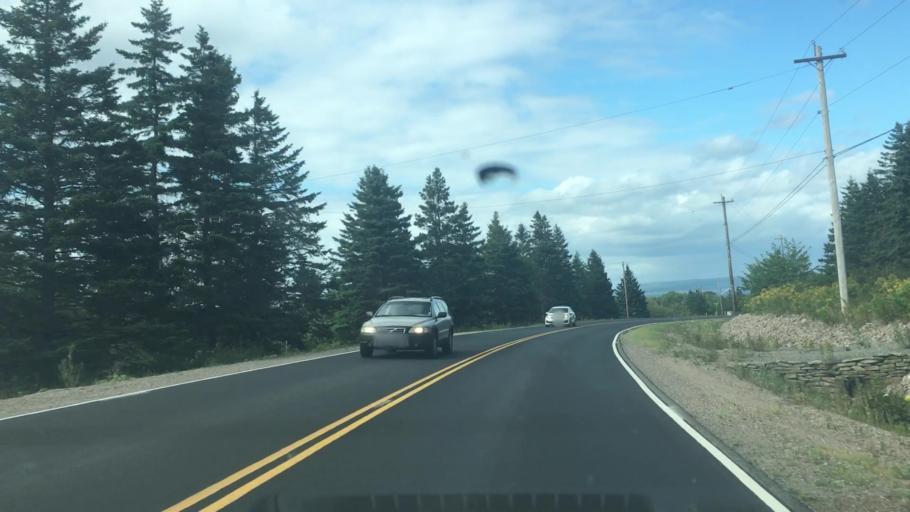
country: CA
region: Nova Scotia
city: Princeville
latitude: 45.7891
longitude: -60.7406
